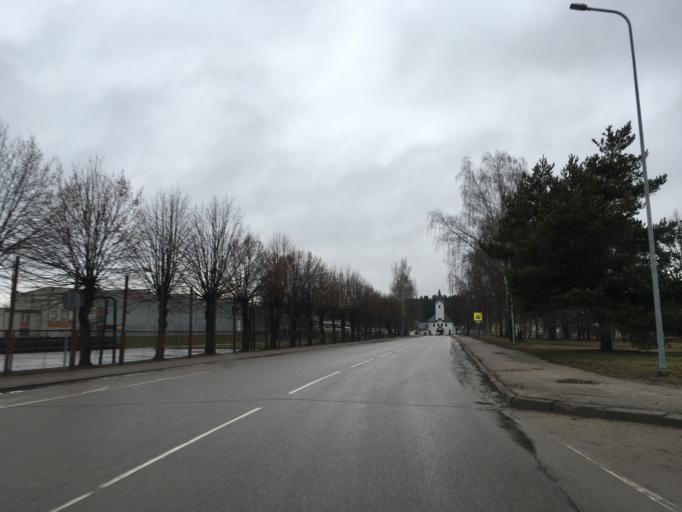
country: LV
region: Ozolnieku
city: Ozolnieki
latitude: 56.6907
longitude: 23.7924
